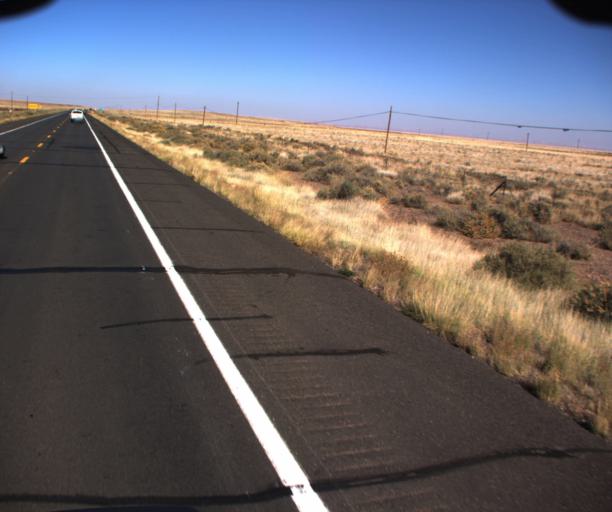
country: US
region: Arizona
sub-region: Coconino County
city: Flagstaff
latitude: 35.6823
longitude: -111.5068
